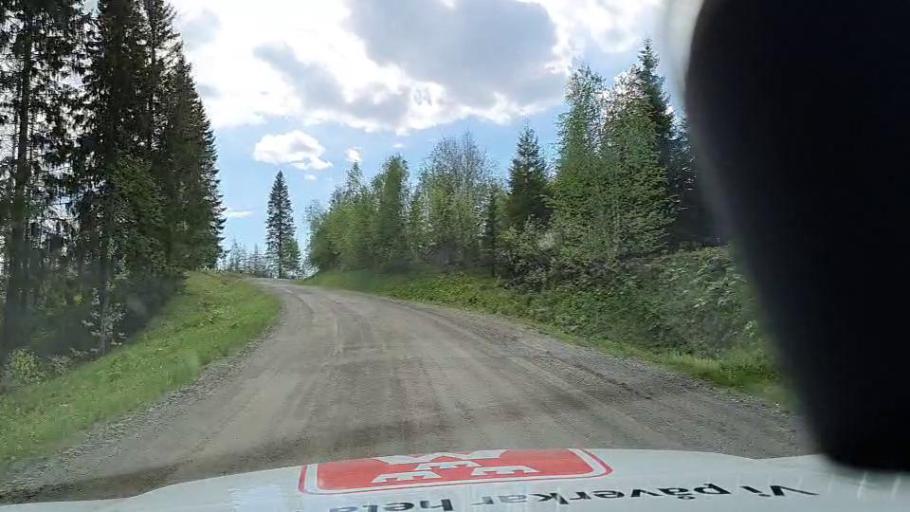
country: SE
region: Vaesterbotten
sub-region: Vilhelmina Kommun
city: Sjoberg
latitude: 64.5613
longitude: 15.8468
